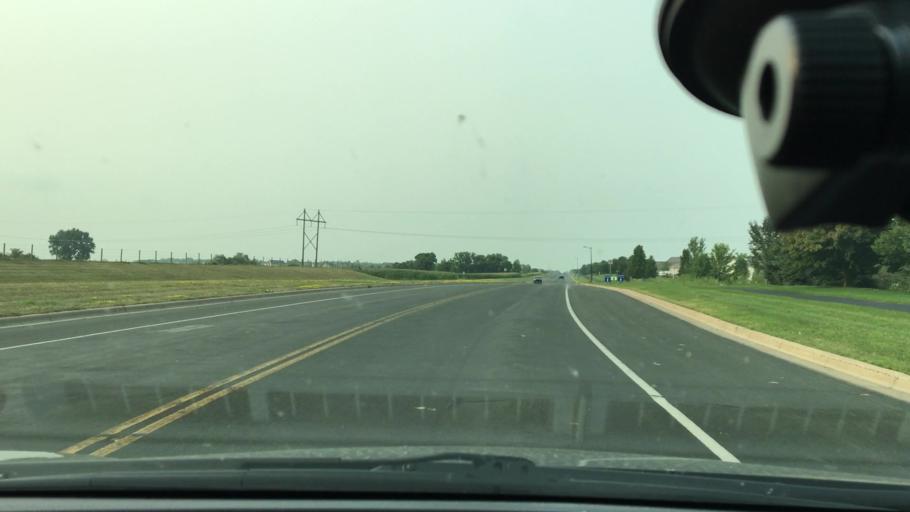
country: US
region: Minnesota
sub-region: Wright County
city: Albertville
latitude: 45.2413
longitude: -93.6427
